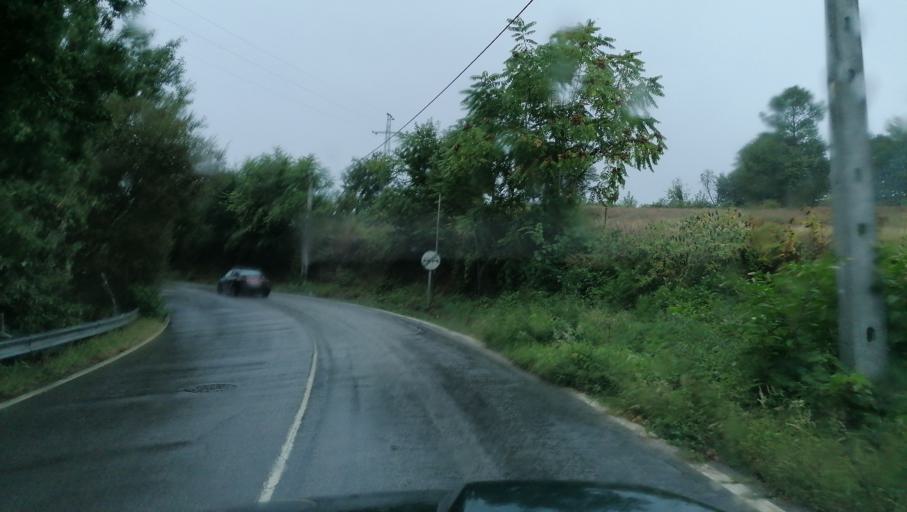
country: PT
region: Braga
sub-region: Cabeceiras de Basto
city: Cabeceiras de Basto
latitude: 41.4997
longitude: -7.9090
